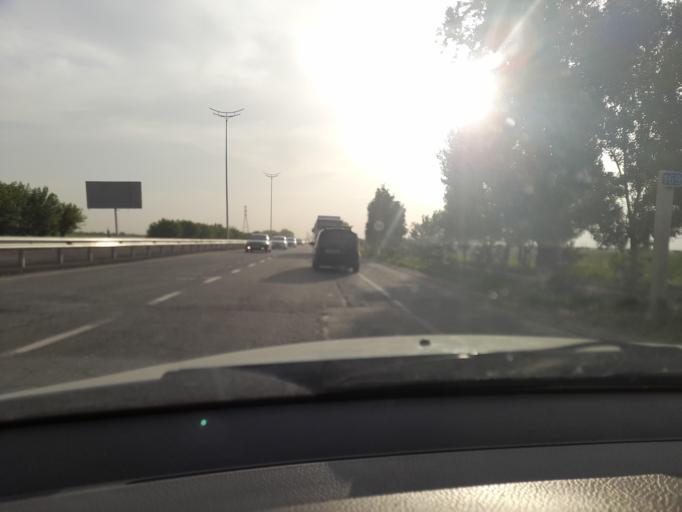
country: UZ
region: Navoiy
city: Beshrabot
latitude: 40.1343
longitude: 65.2386
